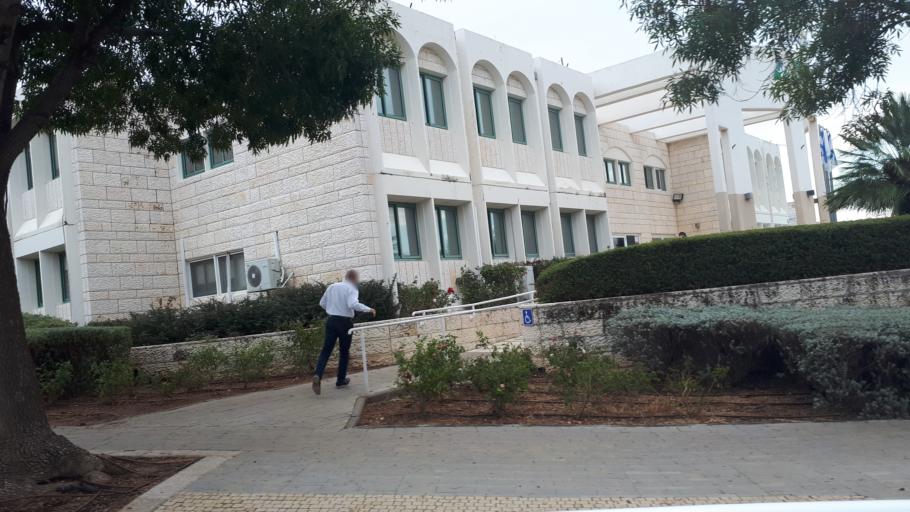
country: IL
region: Central District
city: Modiin
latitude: 31.9078
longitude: 35.0072
